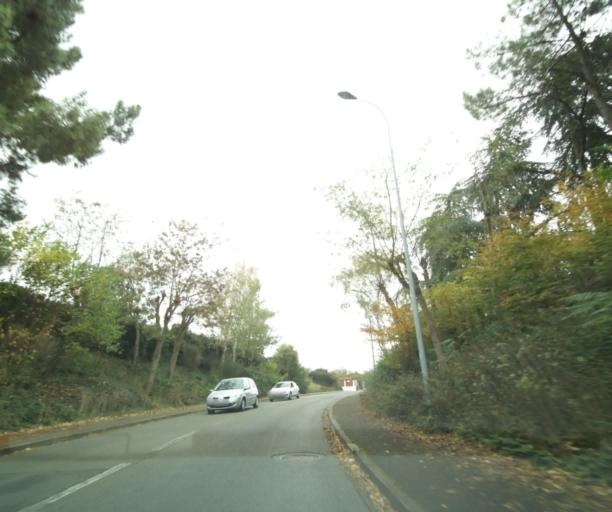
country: FR
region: Centre
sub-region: Departement d'Eure-et-Loir
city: Dreux
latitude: 48.7343
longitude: 1.3471
